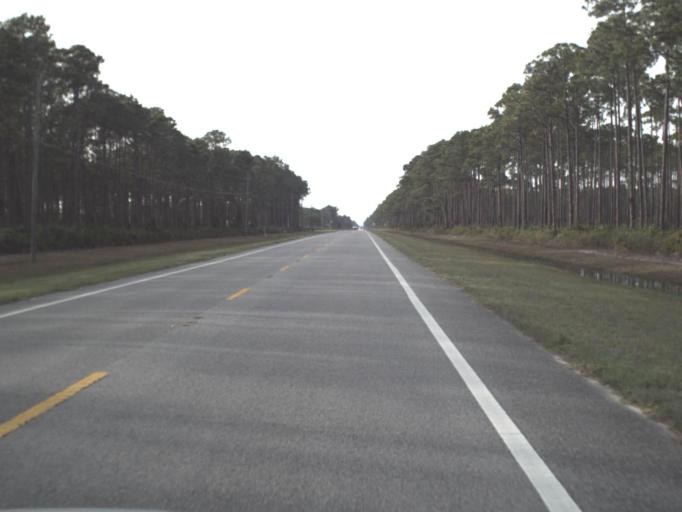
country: US
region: Florida
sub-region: Bay County
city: Tyndall Air Force Base
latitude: 30.0284
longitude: -85.5362
